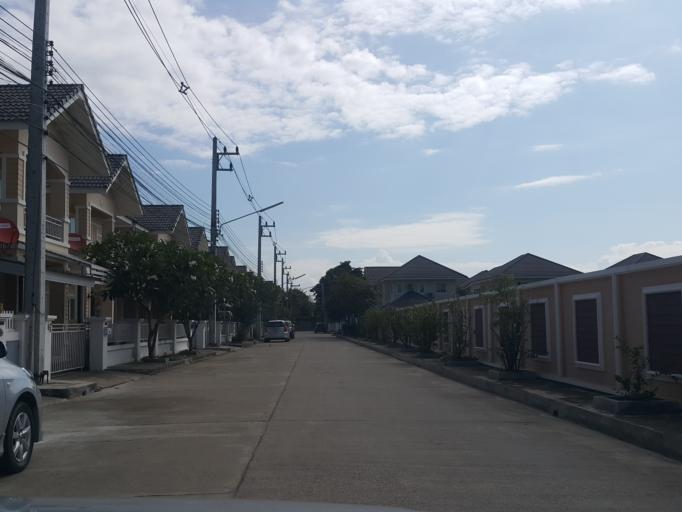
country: TH
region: Chiang Mai
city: Saraphi
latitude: 18.7383
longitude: 99.0453
